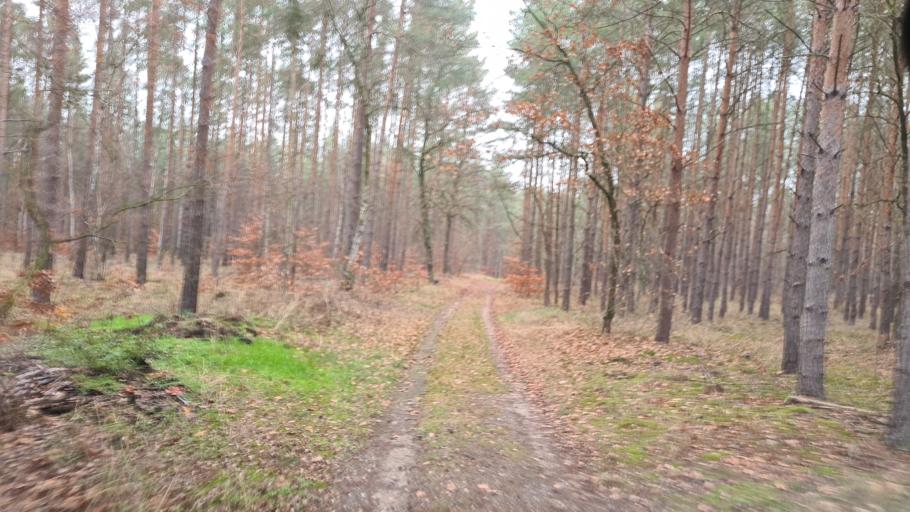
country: DE
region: Brandenburg
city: Doberlug-Kirchhain
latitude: 51.6333
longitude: 13.5299
